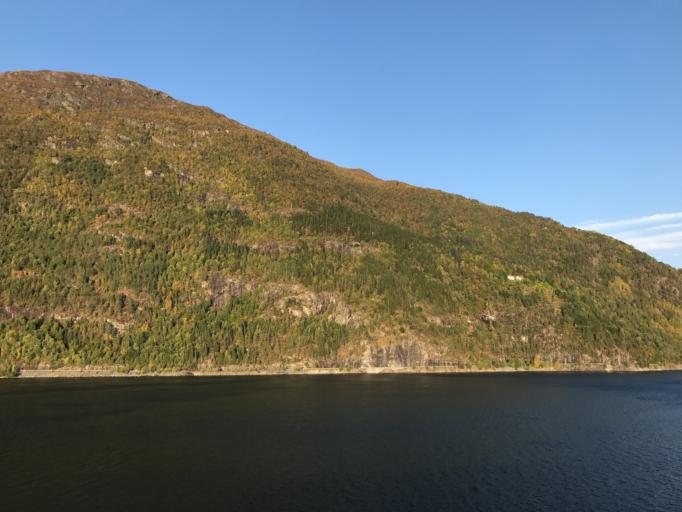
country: NO
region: Sogn og Fjordane
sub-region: Gloppen
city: Sandane
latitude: 61.8494
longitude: 6.1065
